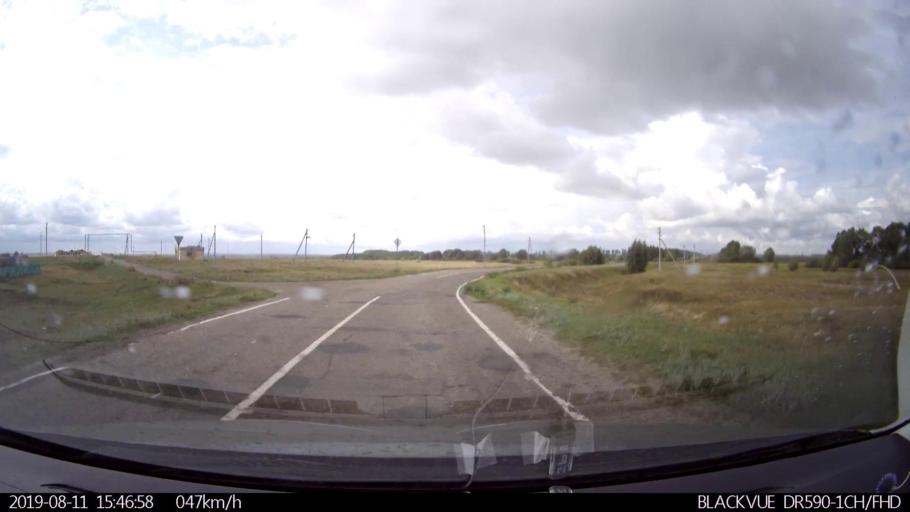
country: RU
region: Ulyanovsk
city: Ignatovka
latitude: 53.8855
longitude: 47.6518
